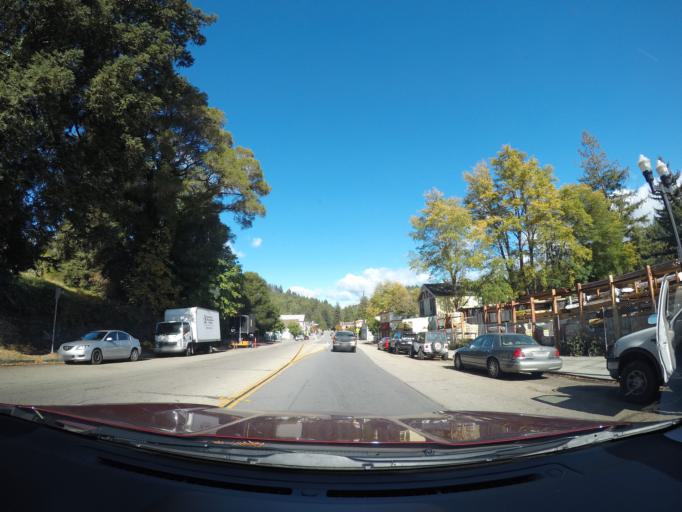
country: US
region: California
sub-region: Santa Cruz County
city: Boulder Creek
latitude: 37.1227
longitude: -122.1214
